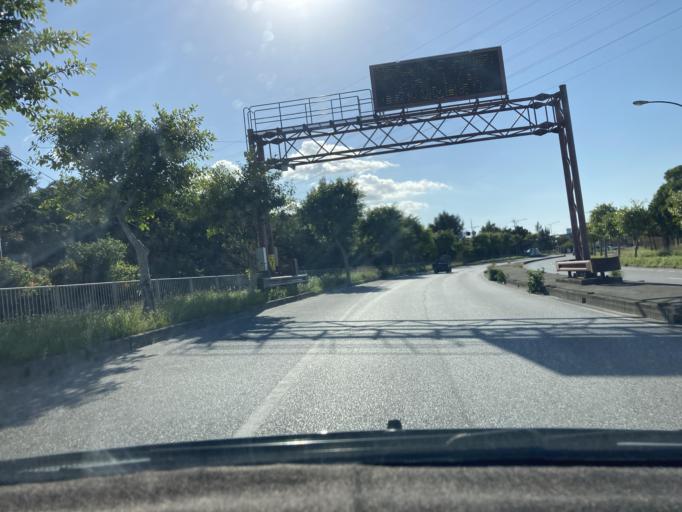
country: JP
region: Okinawa
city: Ishikawa
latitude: 26.4355
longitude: 127.8409
